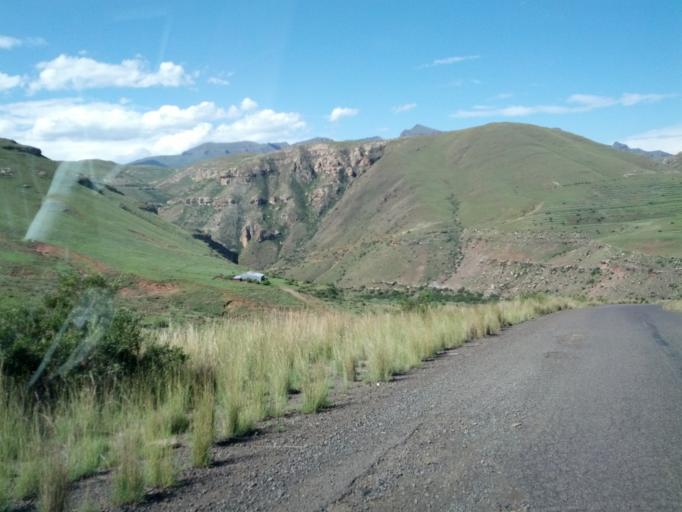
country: LS
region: Qacha's Nek
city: Qacha's Nek
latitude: -30.0531
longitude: 28.4996
